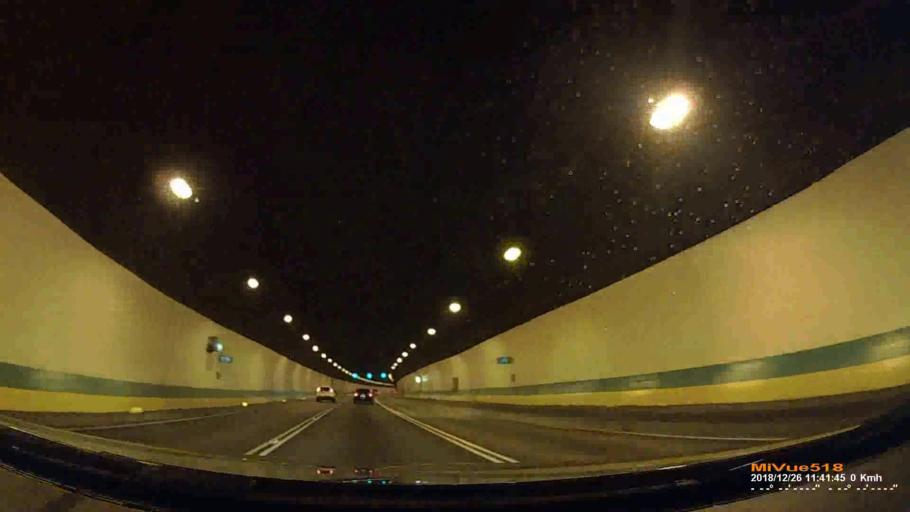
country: TW
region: Taipei
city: Taipei
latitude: 25.0263
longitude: 121.6052
